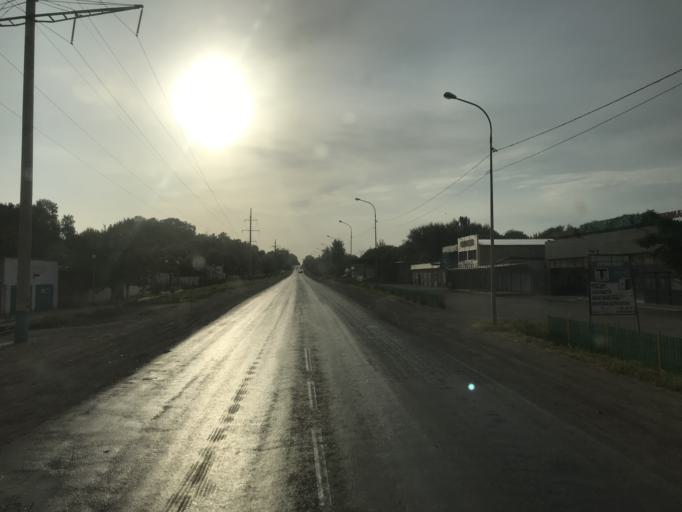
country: KZ
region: Ongtustik Qazaqstan
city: Saryaghash
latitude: 41.4899
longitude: 69.2625
